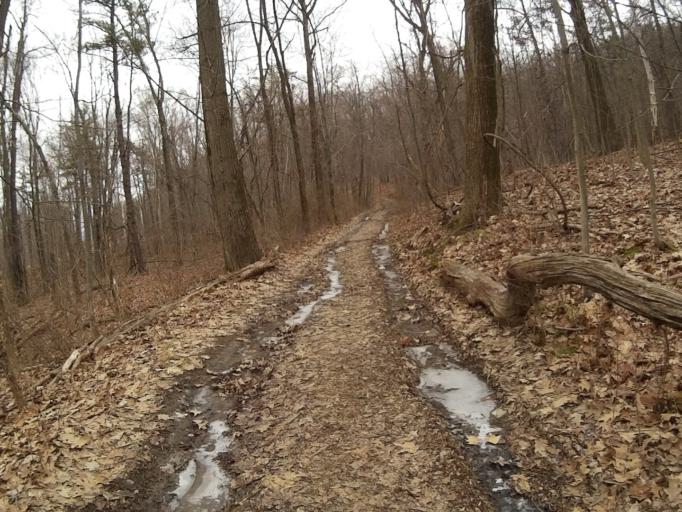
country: US
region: Pennsylvania
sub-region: Centre County
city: Lemont
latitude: 40.8142
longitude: -77.8037
